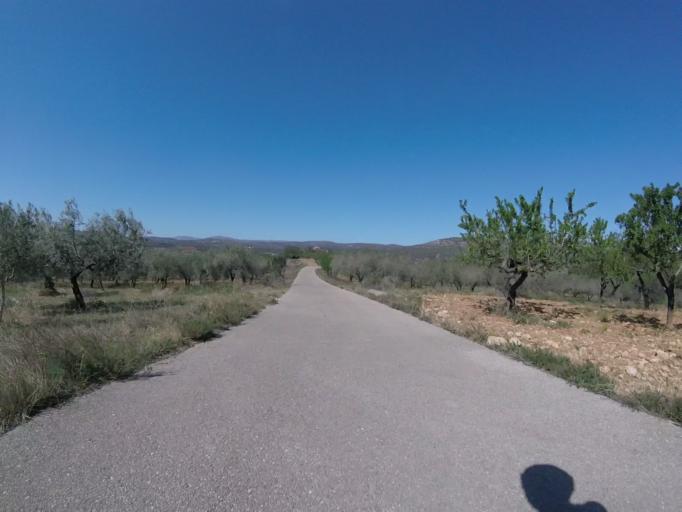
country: ES
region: Valencia
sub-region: Provincia de Castello
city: Cuevas de Vinroma
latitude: 40.3825
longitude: 0.1525
